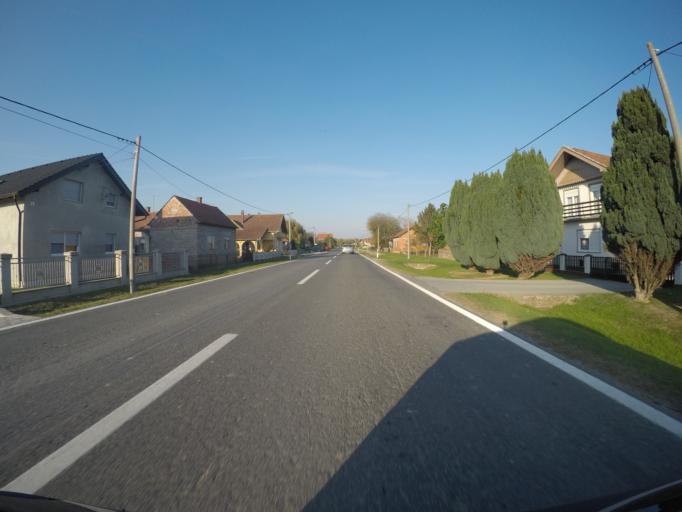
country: HU
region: Somogy
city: Barcs
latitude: 45.9317
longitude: 17.4596
